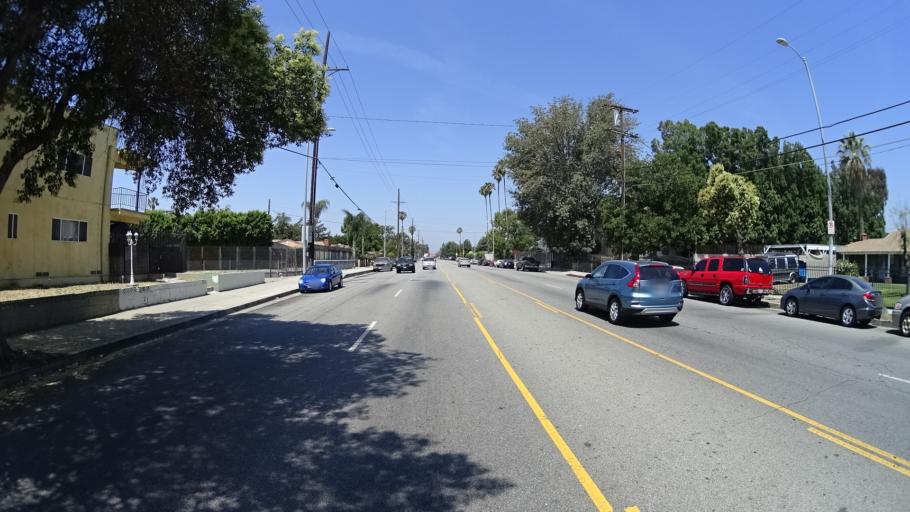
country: US
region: California
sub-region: Los Angeles County
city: Van Nuys
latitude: 34.2084
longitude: -118.4532
